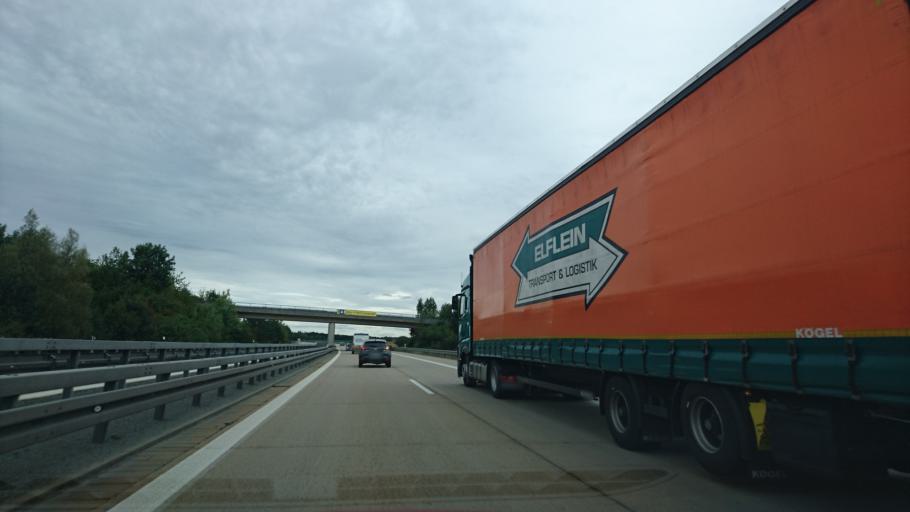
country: DE
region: Bavaria
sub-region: Upper Palatinate
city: Luhe-Wildenau
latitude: 49.6091
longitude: 12.1526
